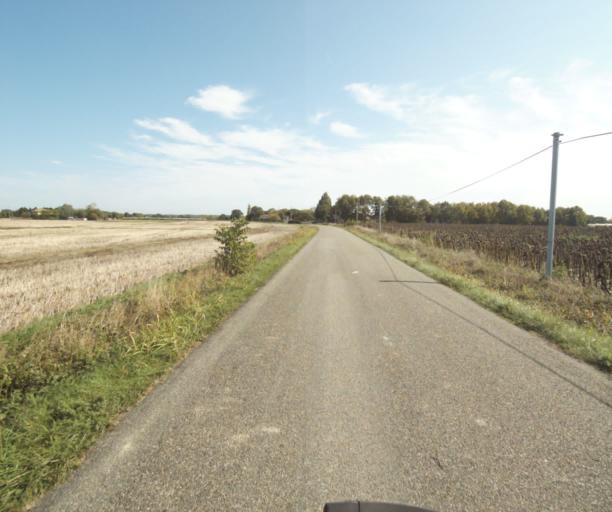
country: FR
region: Midi-Pyrenees
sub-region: Departement du Tarn-et-Garonne
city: Verdun-sur-Garonne
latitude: 43.8557
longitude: 1.2117
